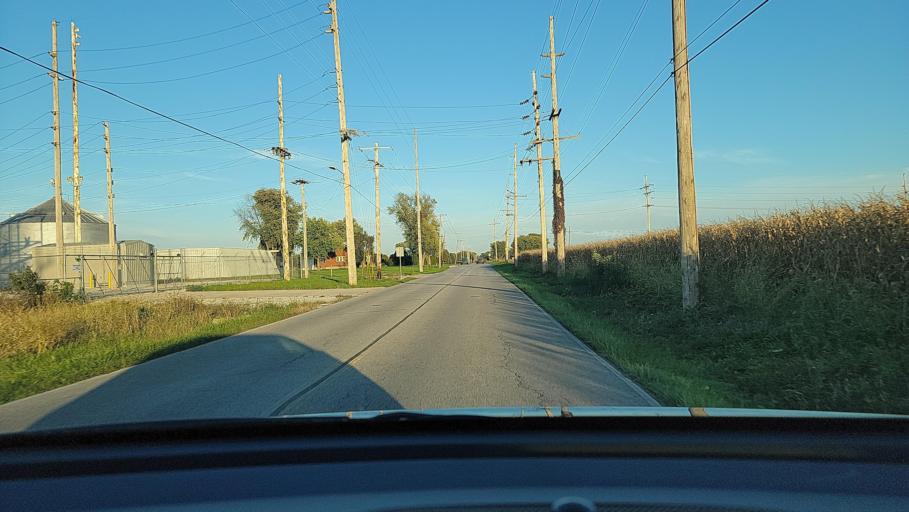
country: US
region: Indiana
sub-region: Porter County
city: Portage
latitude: 41.5360
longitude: -87.1886
